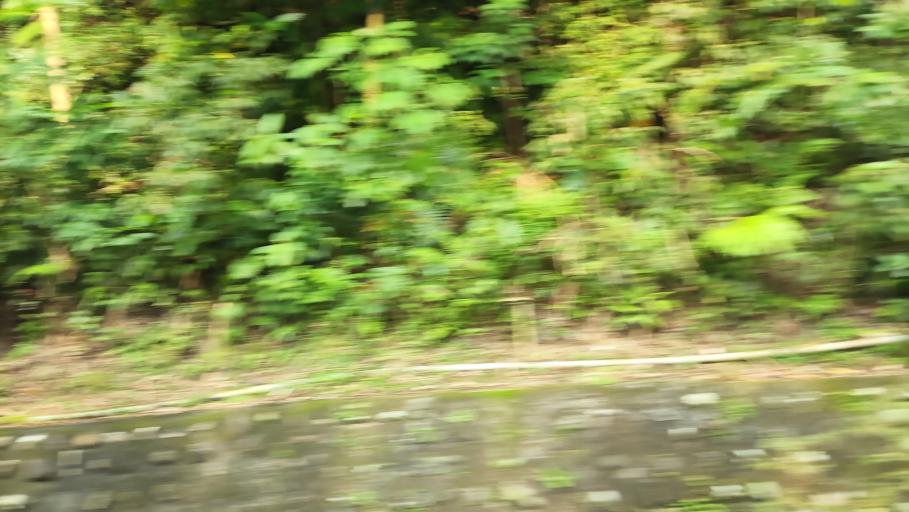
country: TW
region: Taiwan
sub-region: Keelung
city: Keelung
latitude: 25.1493
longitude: 121.6246
